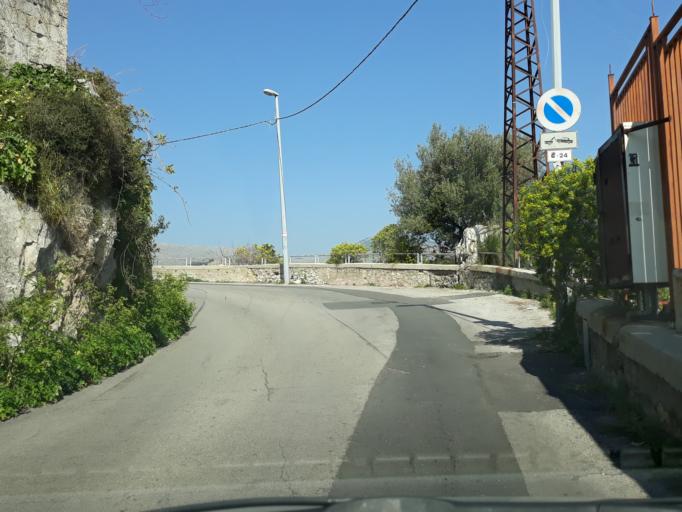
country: IT
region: Sicily
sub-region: Palermo
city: Piano dei Geli
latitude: 38.1100
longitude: 13.3065
